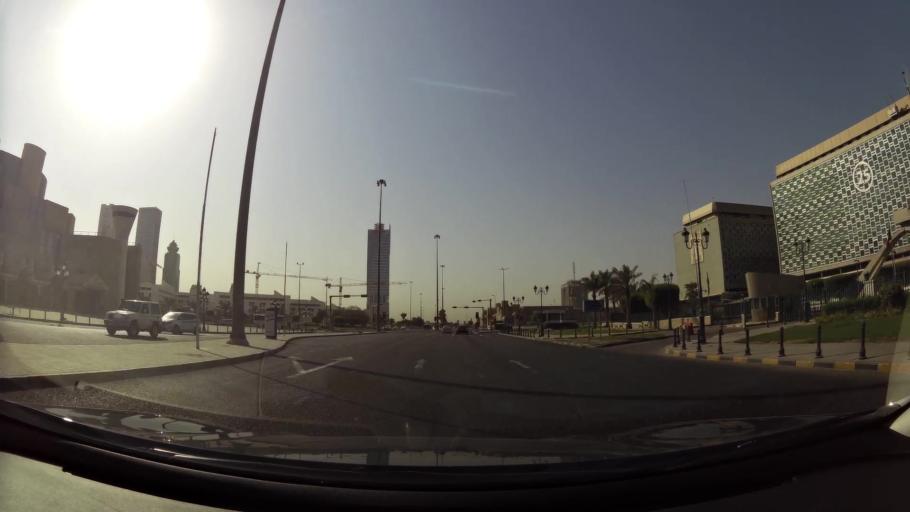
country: KW
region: Al Asimah
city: Kuwait City
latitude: 29.3680
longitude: 47.9741
